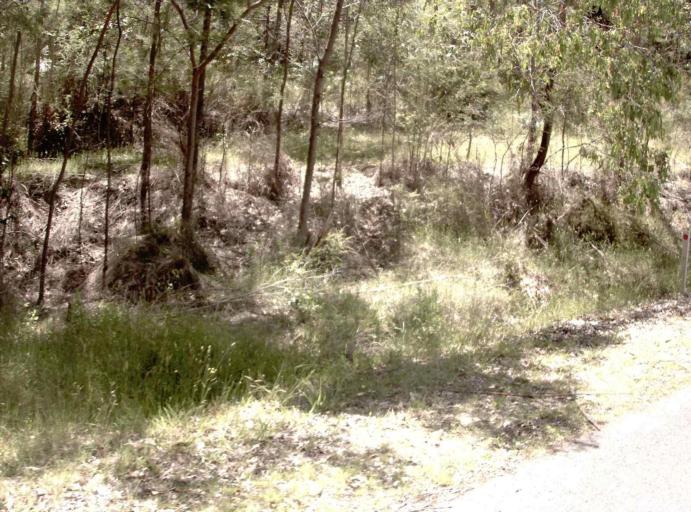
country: AU
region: New South Wales
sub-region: Bombala
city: Bombala
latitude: -37.5182
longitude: 148.9289
